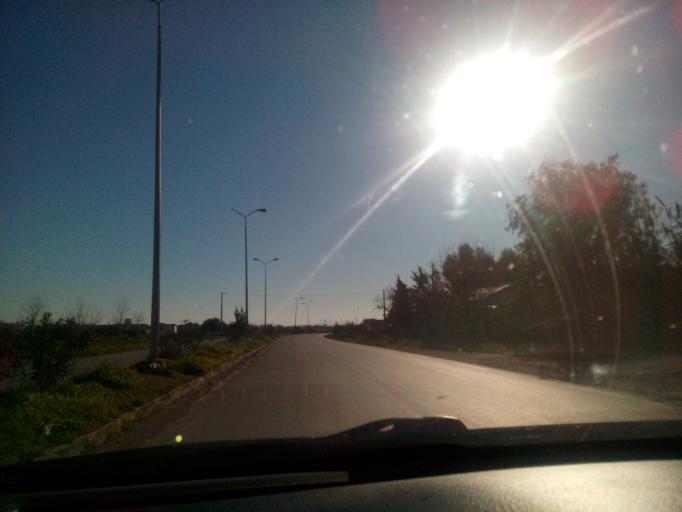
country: DZ
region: Relizane
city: Relizane
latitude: 35.7198
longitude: 0.5760
